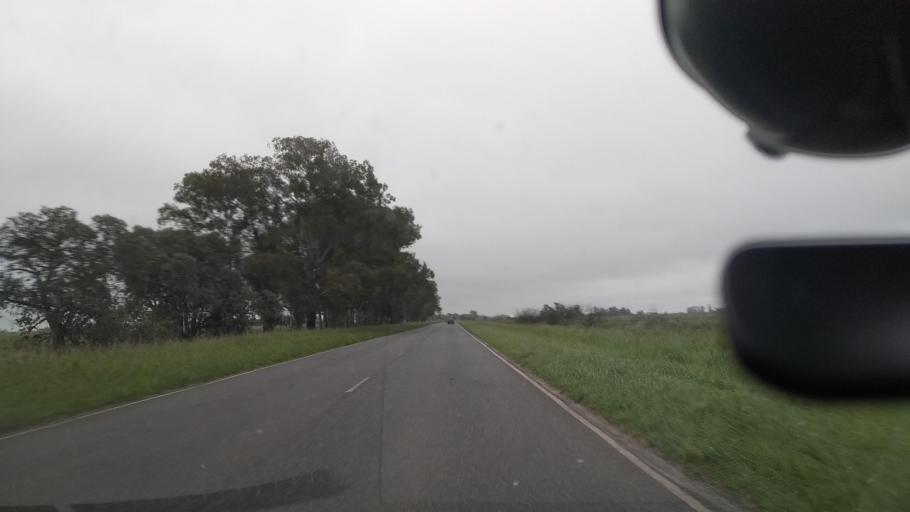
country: AR
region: Buenos Aires
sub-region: Partido de Magdalena
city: Magdalena
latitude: -35.2344
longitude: -57.7018
